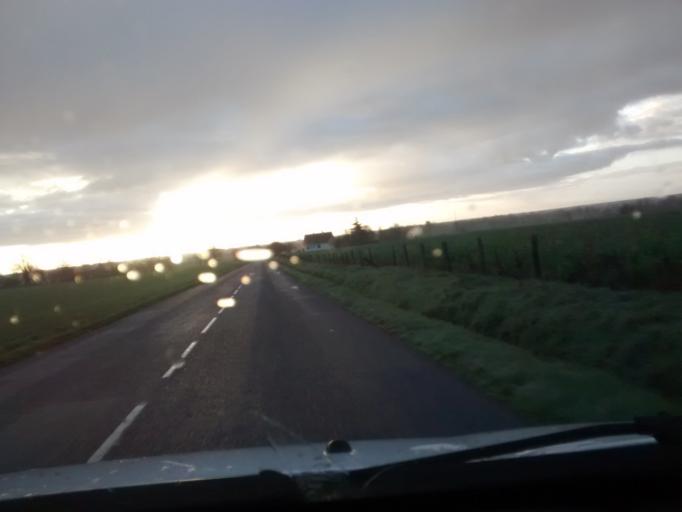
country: FR
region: Brittany
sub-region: Departement d'Ille-et-Vilaine
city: Bais
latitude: 47.9793
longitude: -1.2749
